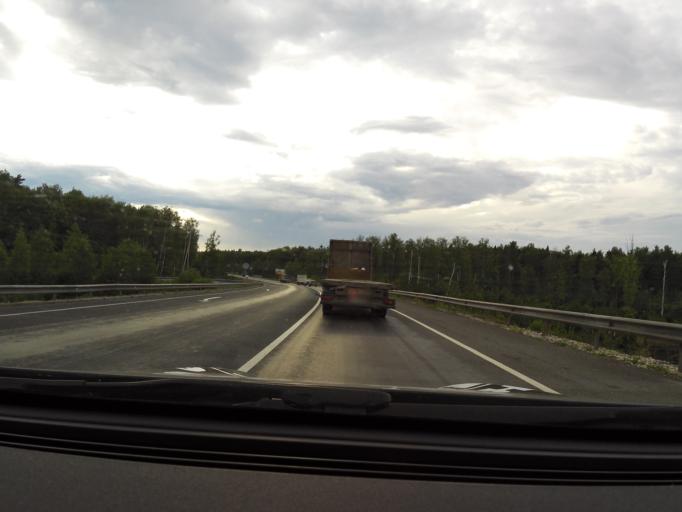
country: RU
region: Vladimir
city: Raduzhnyy
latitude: 56.0644
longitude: 40.3651
